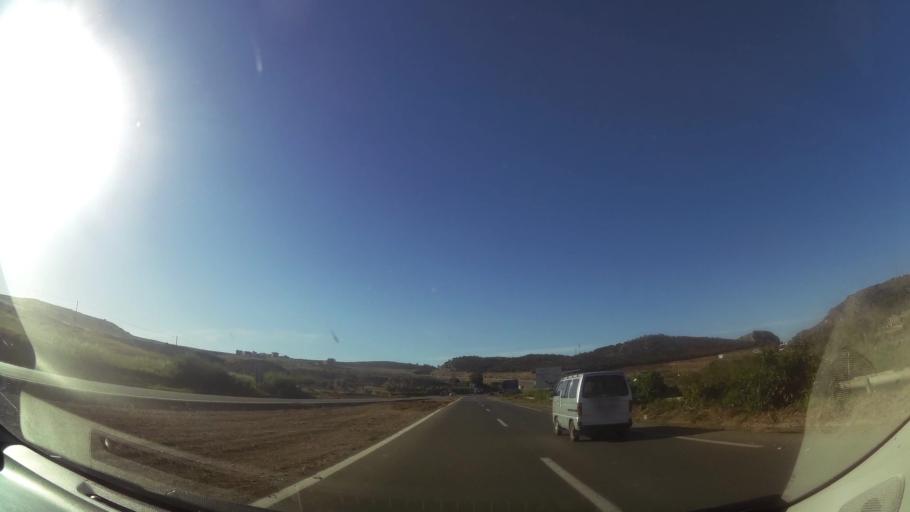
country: MA
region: Oriental
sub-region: Berkane-Taourirt
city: Madagh
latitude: 35.0475
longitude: -2.2189
